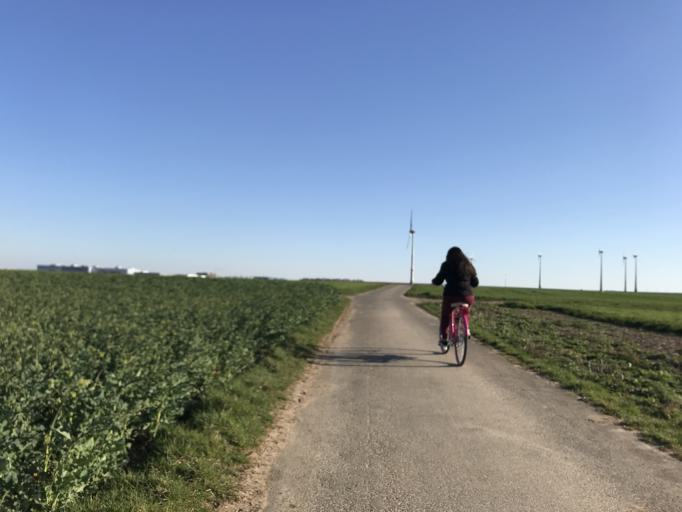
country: DE
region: Rheinland-Pfalz
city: Klein-Winternheim
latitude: 49.9564
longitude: 8.2400
